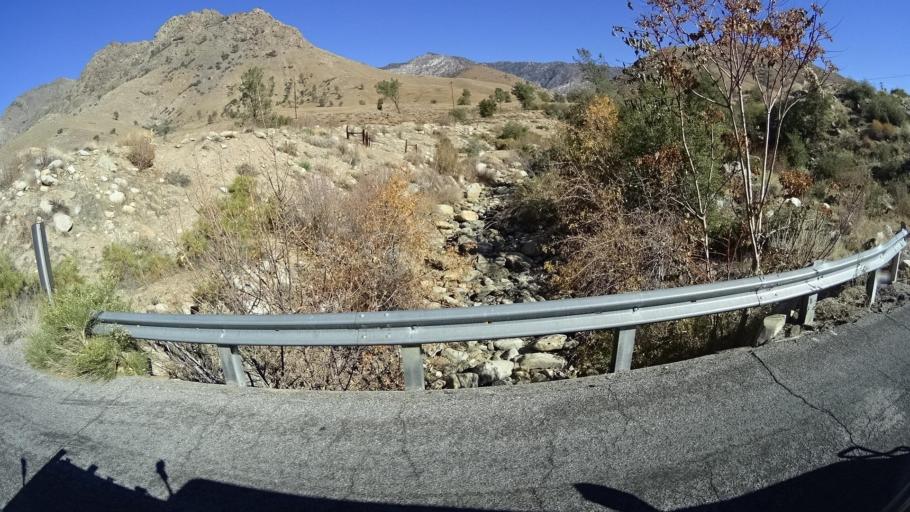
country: US
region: California
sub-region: Kern County
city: Kernville
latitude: 35.7932
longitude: -118.4480
